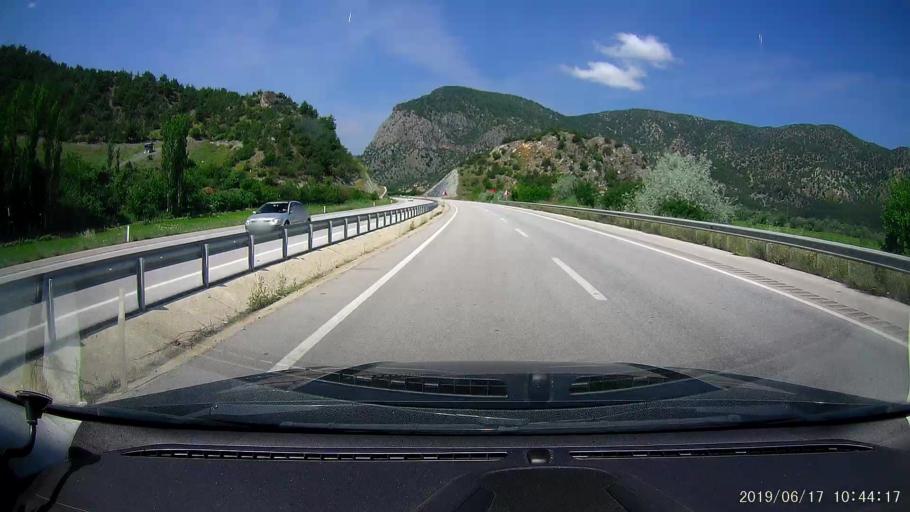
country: TR
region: Corum
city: Hacihamza
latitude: 41.0724
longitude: 34.5161
